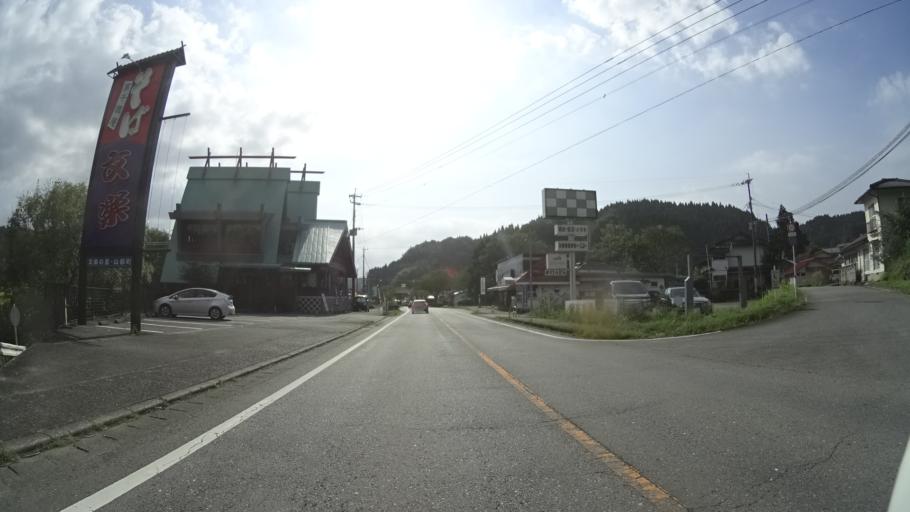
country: JP
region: Kumamoto
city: Aso
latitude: 32.6899
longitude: 131.0894
